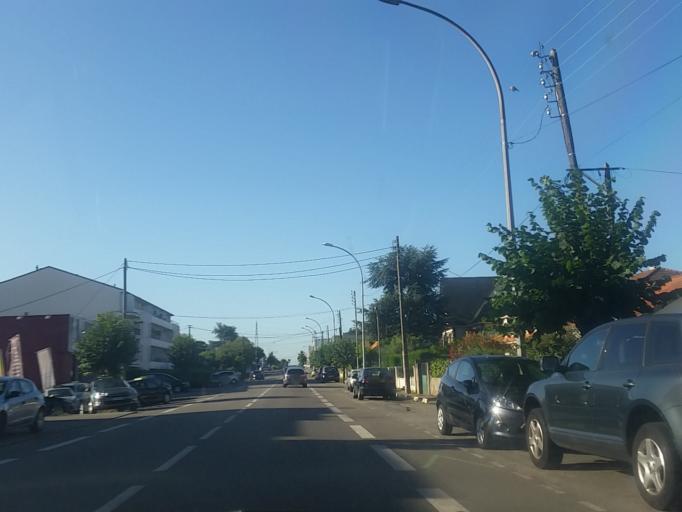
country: FR
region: Pays de la Loire
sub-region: Departement de la Loire-Atlantique
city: Reze
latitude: 47.1707
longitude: -1.5433
